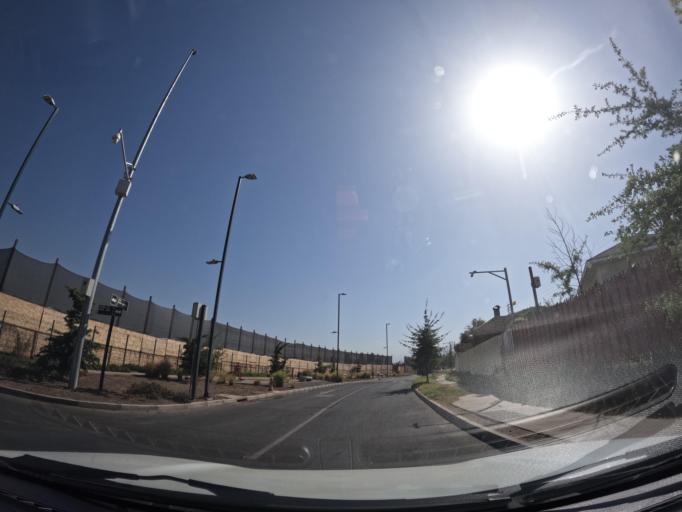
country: CL
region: Santiago Metropolitan
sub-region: Provincia de Santiago
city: Villa Presidente Frei, Nunoa, Santiago, Chile
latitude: -33.4951
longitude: -70.5576
